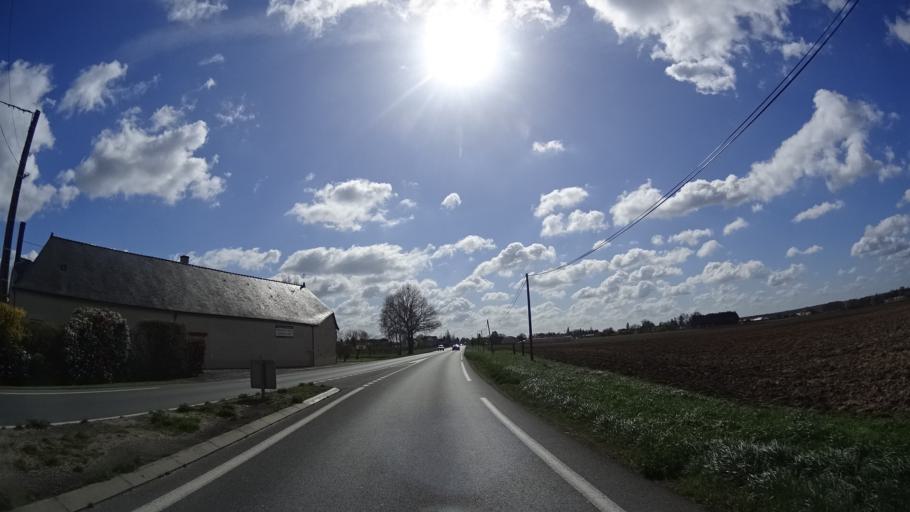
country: FR
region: Pays de la Loire
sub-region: Departement de Maine-et-Loire
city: Brissac-Quince
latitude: 47.3252
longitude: -0.4159
